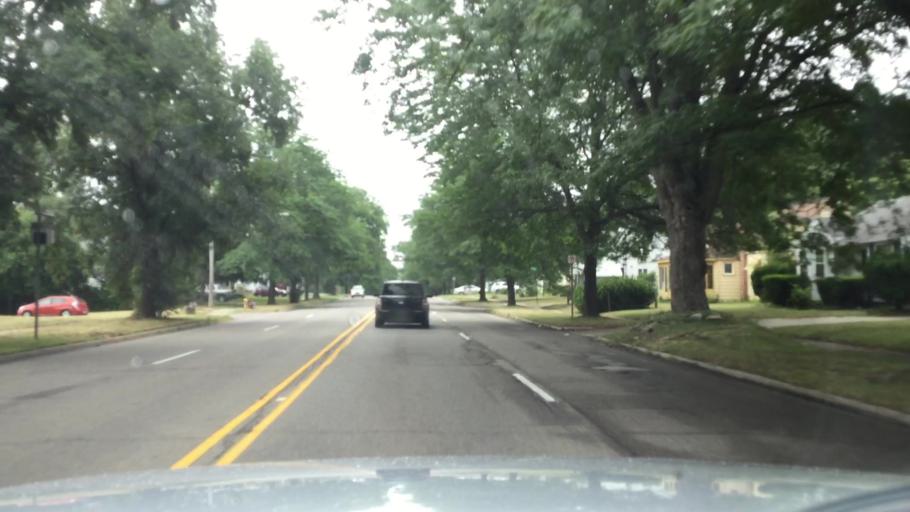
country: US
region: Michigan
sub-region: Genesee County
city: Flint
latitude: 43.0096
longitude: -83.7298
